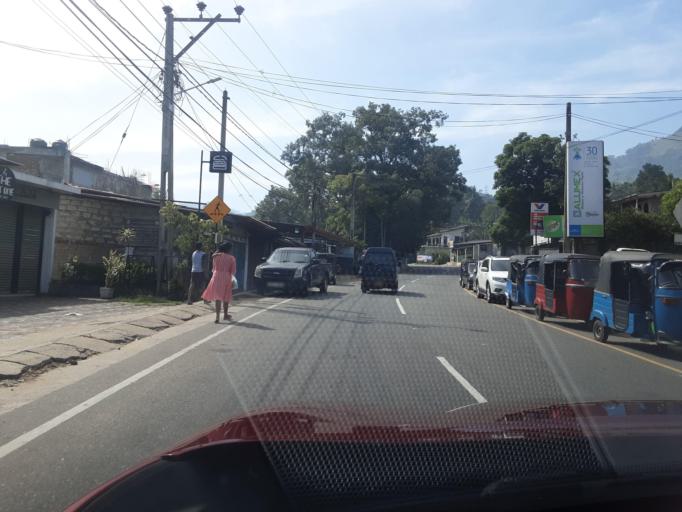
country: LK
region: Uva
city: Badulla
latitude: 6.9853
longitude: 81.0695
